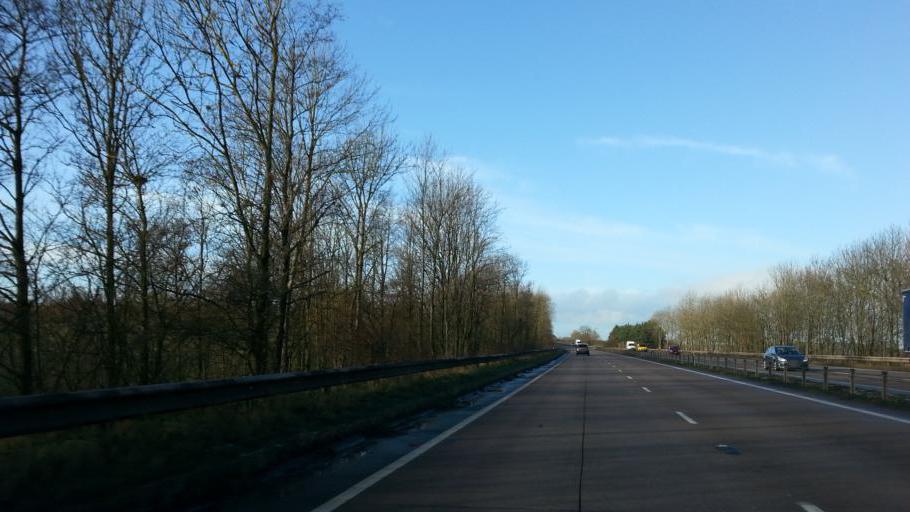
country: GB
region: England
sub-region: Staffordshire
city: Cheadle
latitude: 52.9299
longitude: -1.9513
